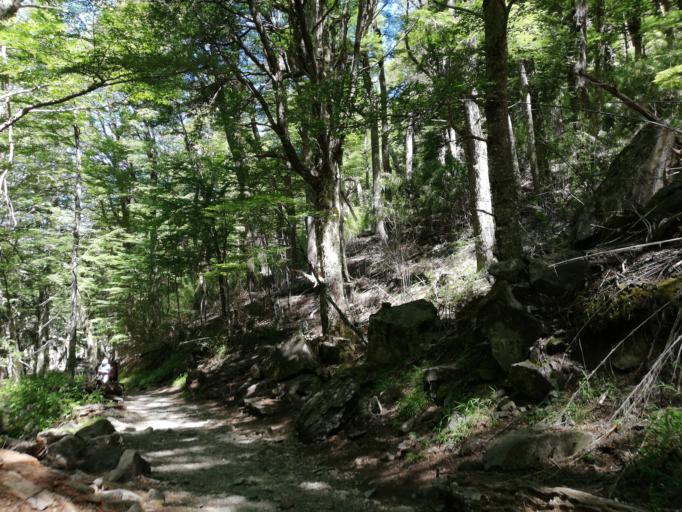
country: AR
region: Neuquen
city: Villa La Angostura
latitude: -41.1924
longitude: -71.8338
